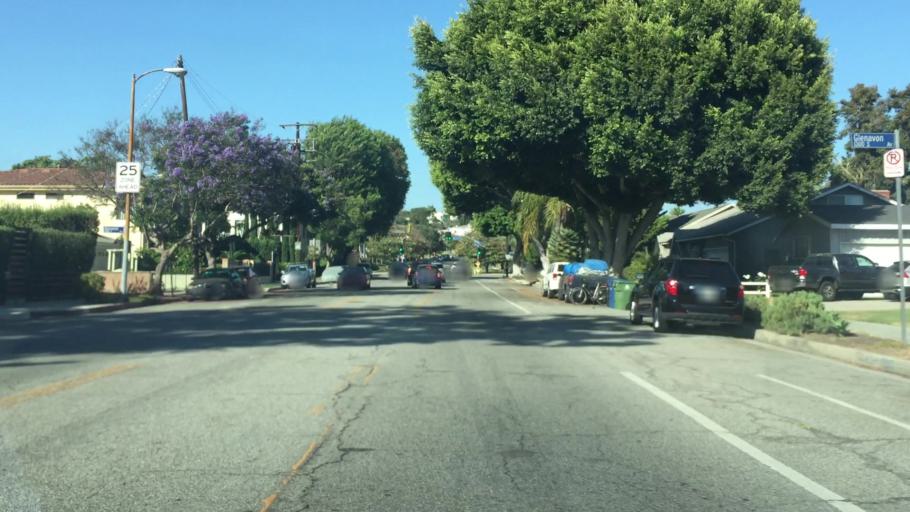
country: US
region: California
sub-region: Los Angeles County
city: Marina del Rey
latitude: 34.0076
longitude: -118.4560
